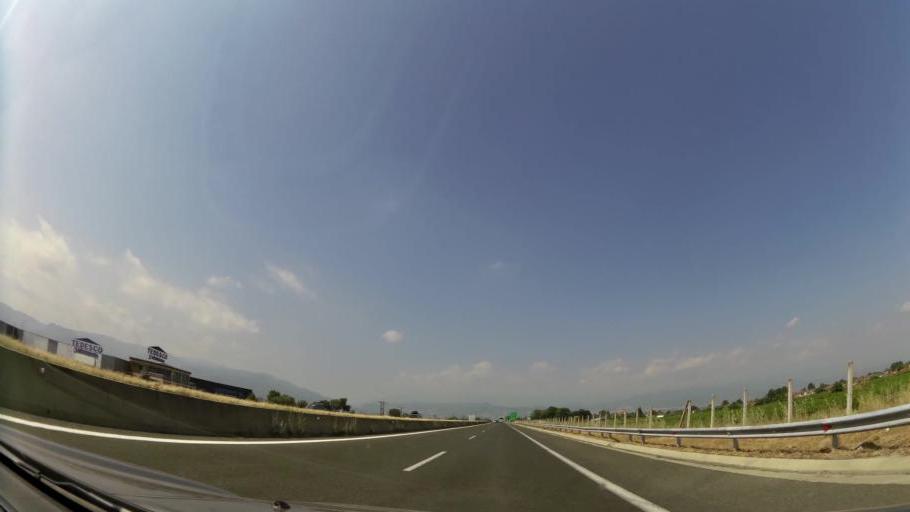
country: GR
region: Central Macedonia
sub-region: Nomos Imathias
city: Kouloura
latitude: 40.5456
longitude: 22.3258
